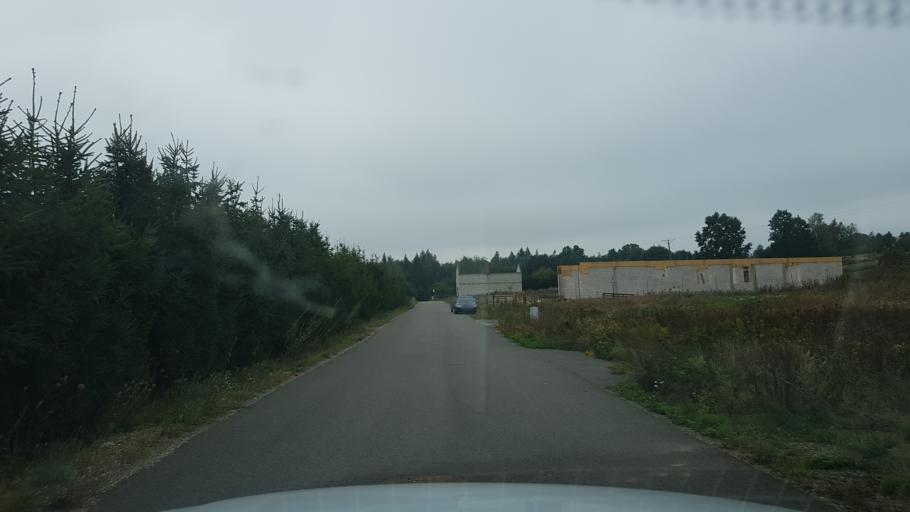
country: PL
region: West Pomeranian Voivodeship
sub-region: Powiat swidwinski
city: Polczyn-Zdroj
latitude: 53.7849
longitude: 16.0706
